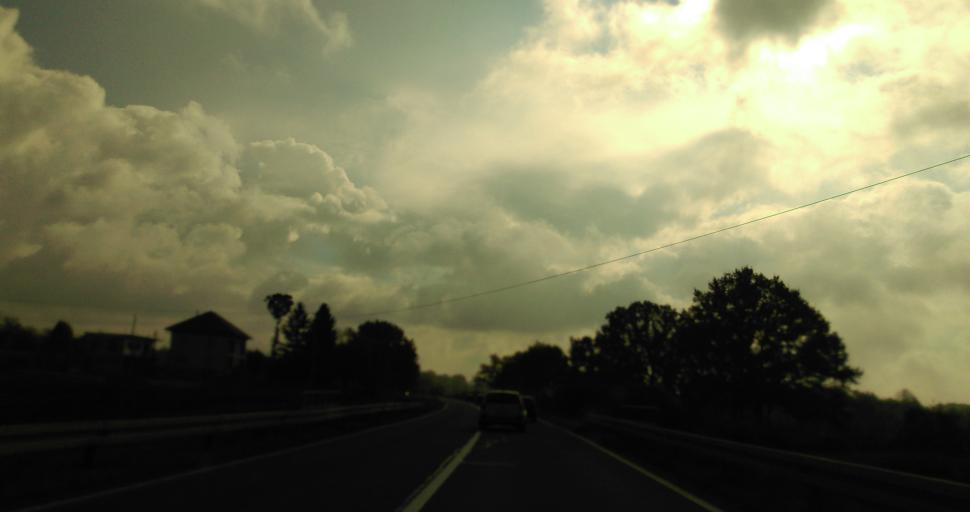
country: RS
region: Central Serbia
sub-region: Belgrade
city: Lazarevac
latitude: 44.3091
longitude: 20.2465
